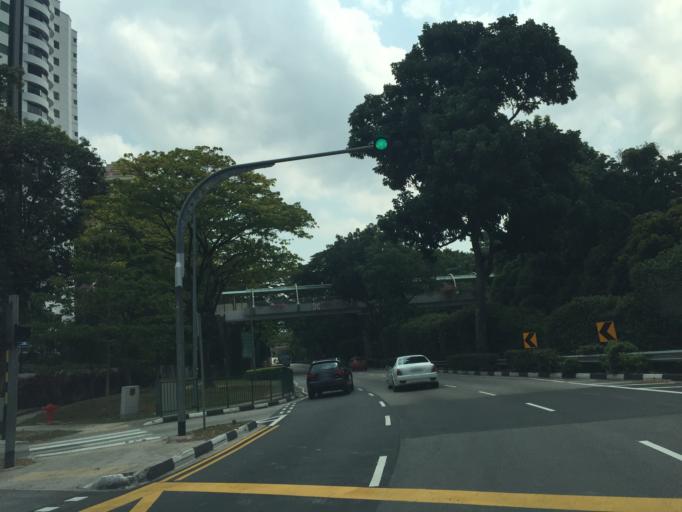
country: SG
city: Singapore
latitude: 1.3172
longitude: 103.8352
